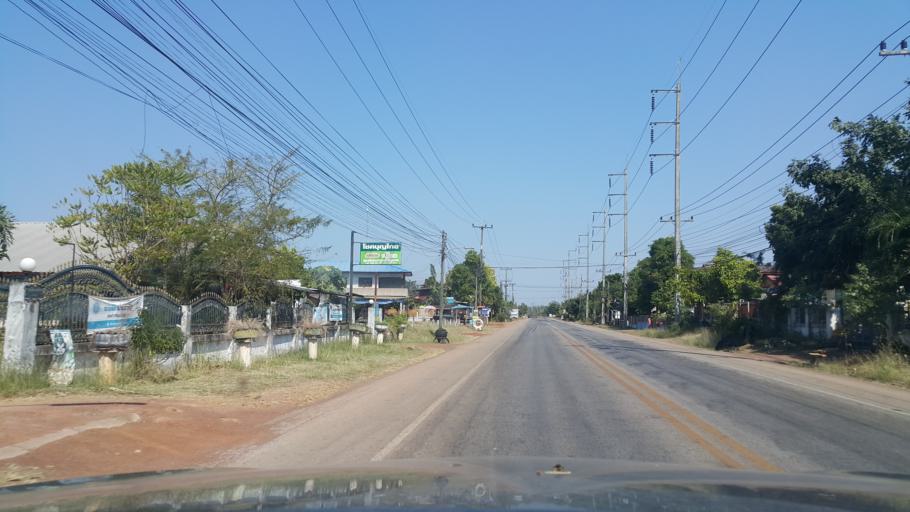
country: TH
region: Changwat Udon Thani
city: Thung Fon
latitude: 17.4545
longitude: 103.1867
